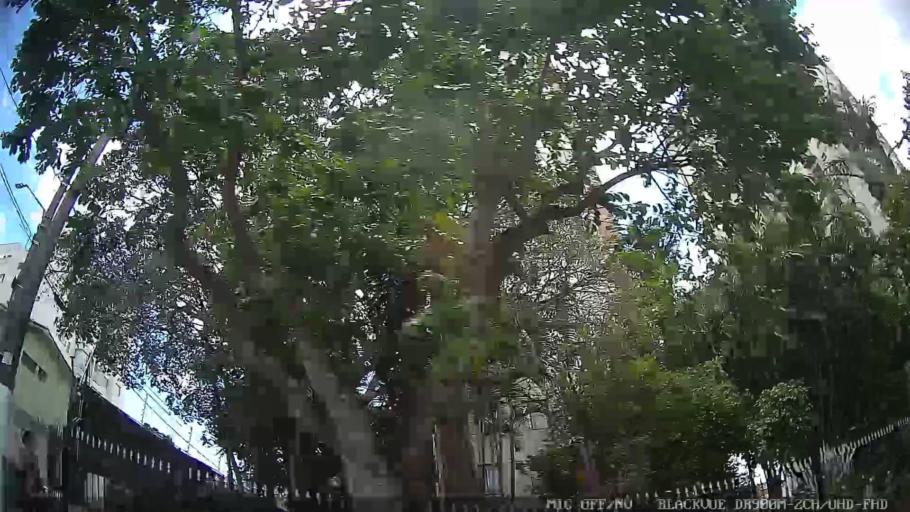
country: BR
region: Sao Paulo
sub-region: Diadema
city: Diadema
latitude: -23.6574
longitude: -46.6490
